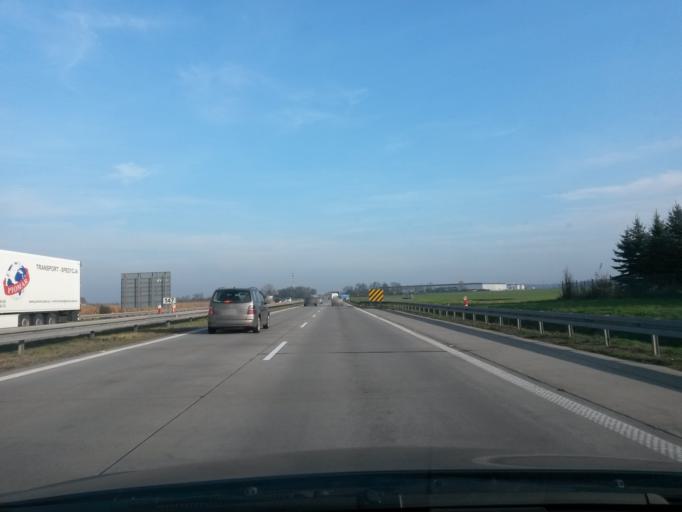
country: PL
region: Lower Silesian Voivodeship
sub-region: Powiat wroclawski
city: Smolec
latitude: 51.0370
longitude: 16.8837
